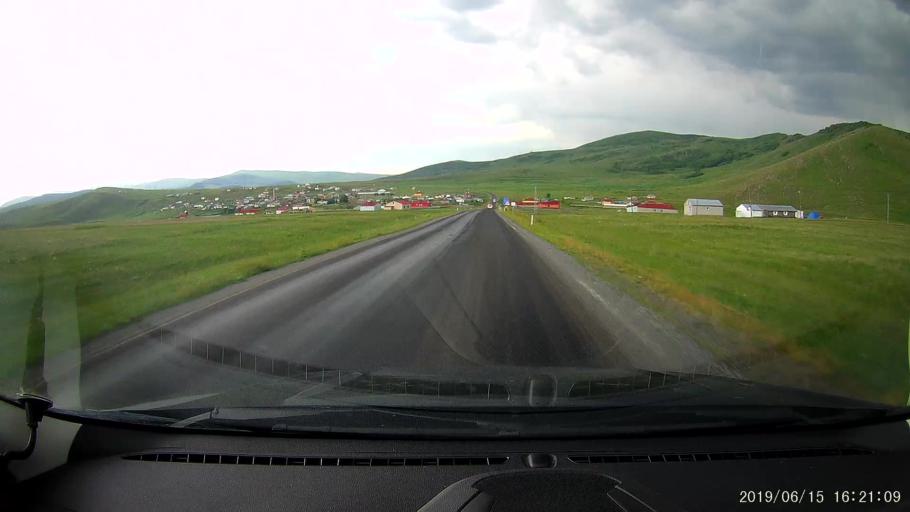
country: TR
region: Ardahan
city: Hanak
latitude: 41.2019
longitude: 42.8461
